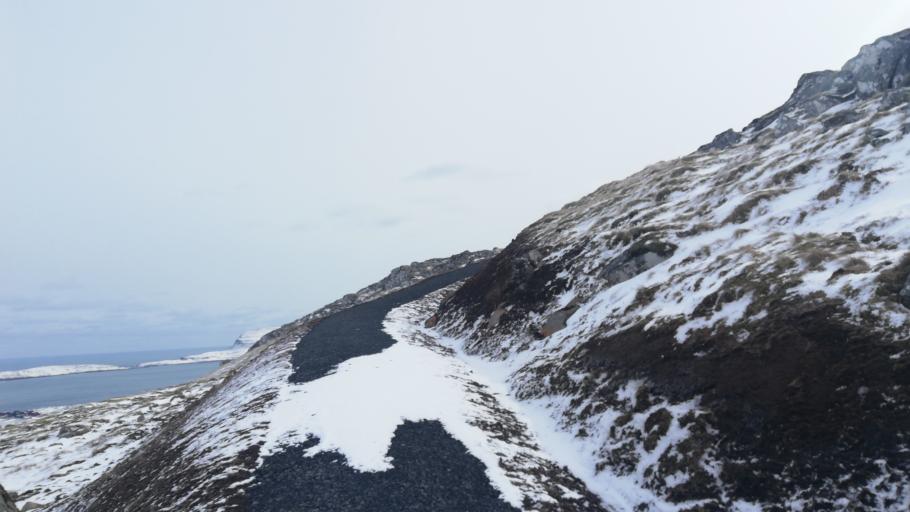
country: FO
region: Streymoy
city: Hoyvik
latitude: 62.0310
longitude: -6.8093
